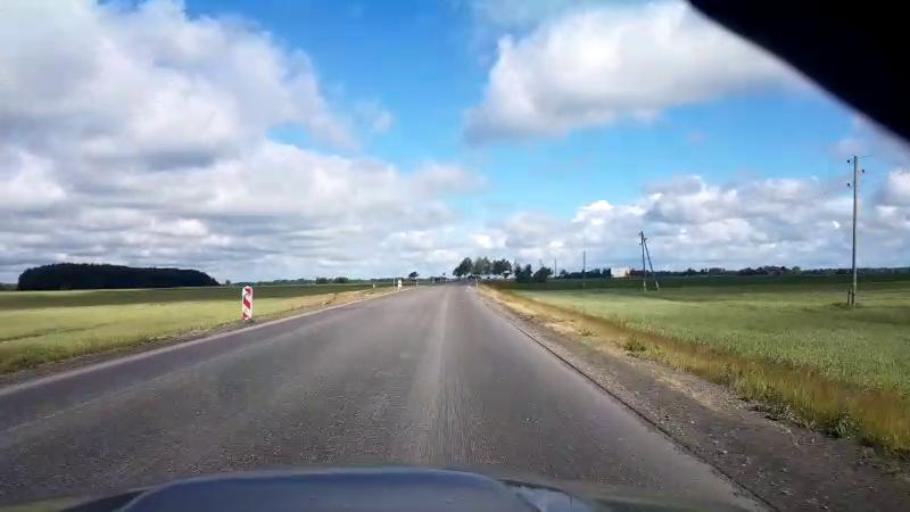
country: LV
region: Bauskas Rajons
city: Bauska
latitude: 56.3316
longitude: 24.3002
